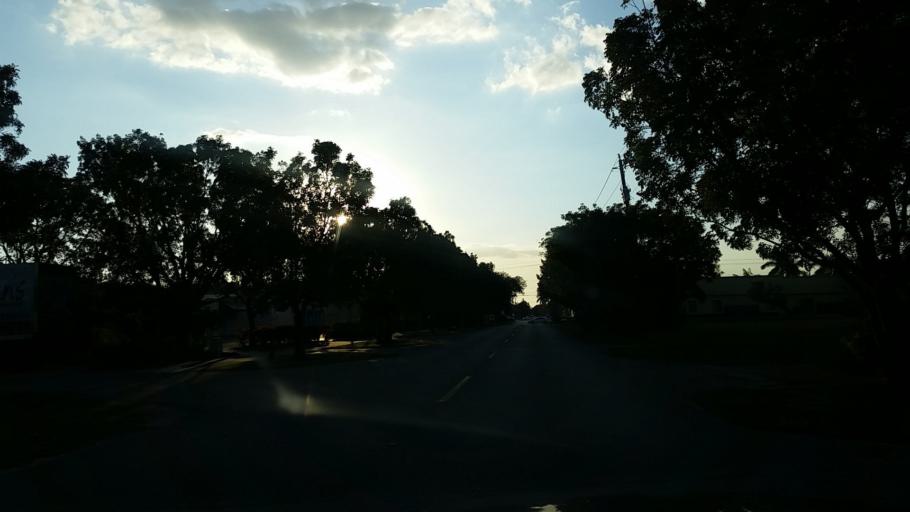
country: US
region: Florida
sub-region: Collier County
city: Naples
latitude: 26.1466
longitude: -81.7924
